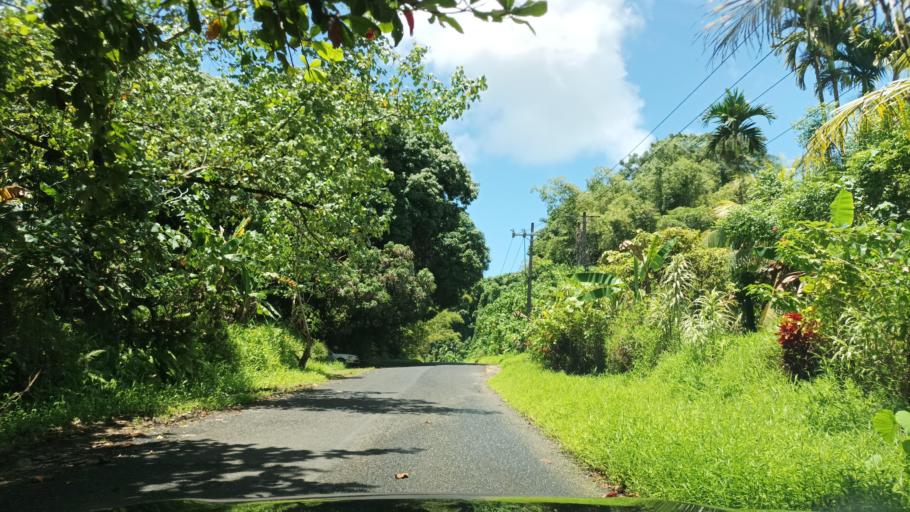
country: FM
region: Pohnpei
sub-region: Madolenihm Municipality
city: Madolenihm Municipality Government
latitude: 6.8504
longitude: 158.2987
